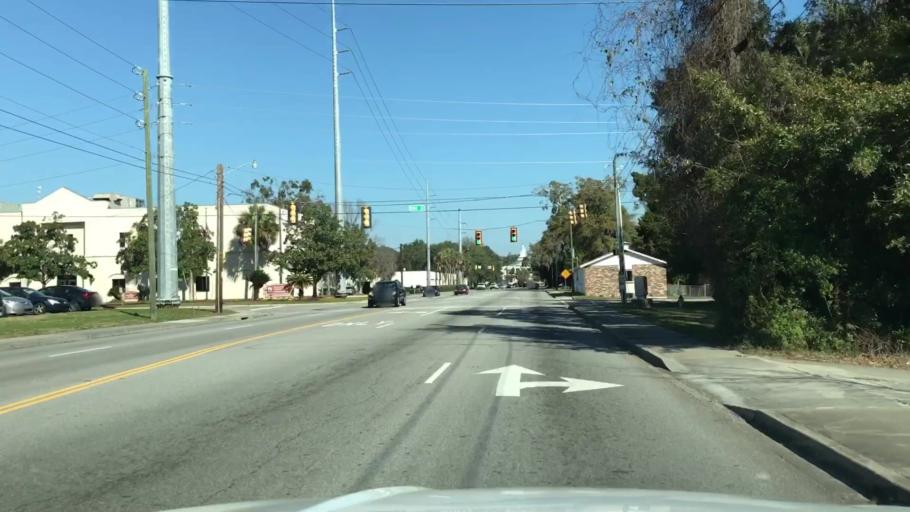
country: US
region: South Carolina
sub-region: Beaufort County
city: Beaufort
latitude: 32.4358
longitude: -80.6860
